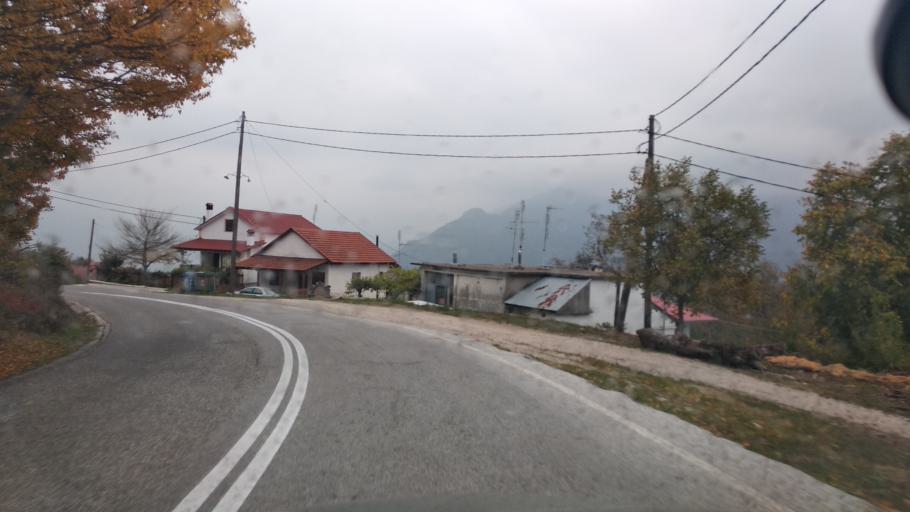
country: GR
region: Thessaly
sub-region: Trikala
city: Pyli
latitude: 39.5077
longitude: 21.5337
